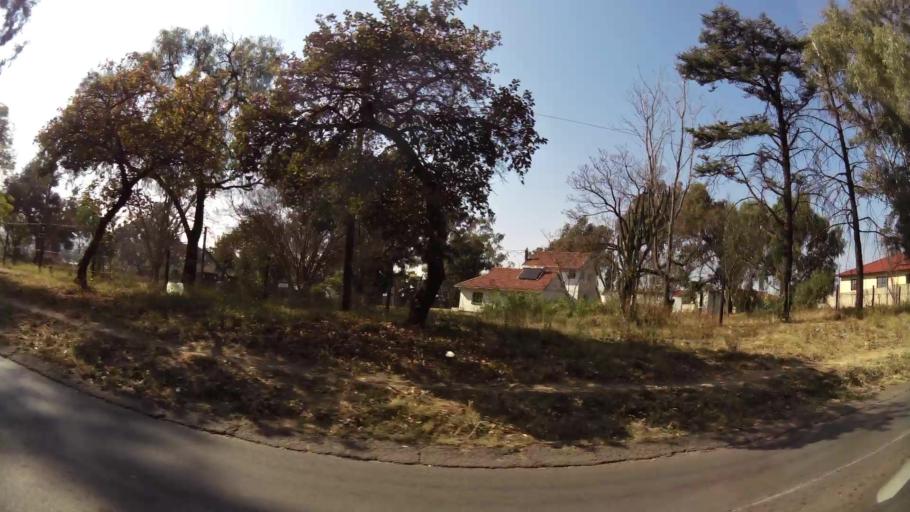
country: ZA
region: Gauteng
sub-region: City of Johannesburg Metropolitan Municipality
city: Modderfontein
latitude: -26.0956
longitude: 28.1324
